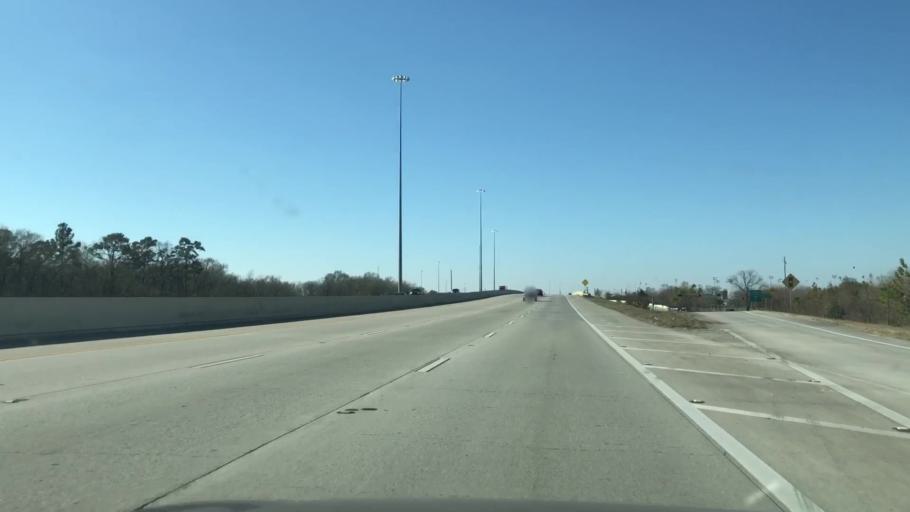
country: US
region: Texas
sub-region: Harris County
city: Jacinto City
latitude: 29.7866
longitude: -95.2436
